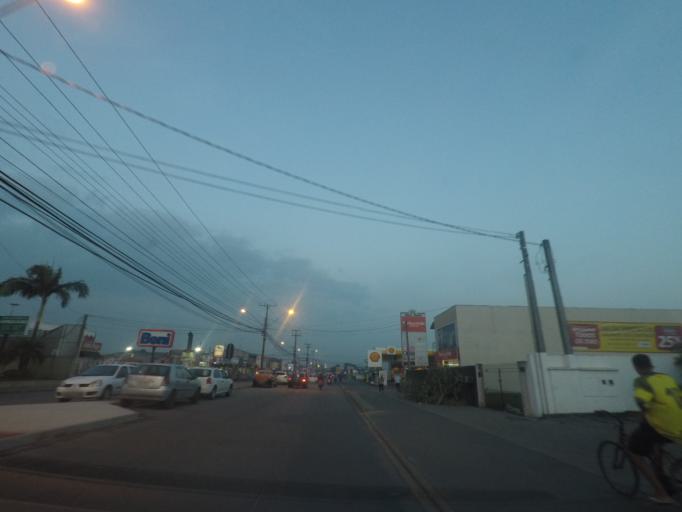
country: BR
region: Parana
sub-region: Pinhais
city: Pinhais
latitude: -25.4507
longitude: -49.1801
